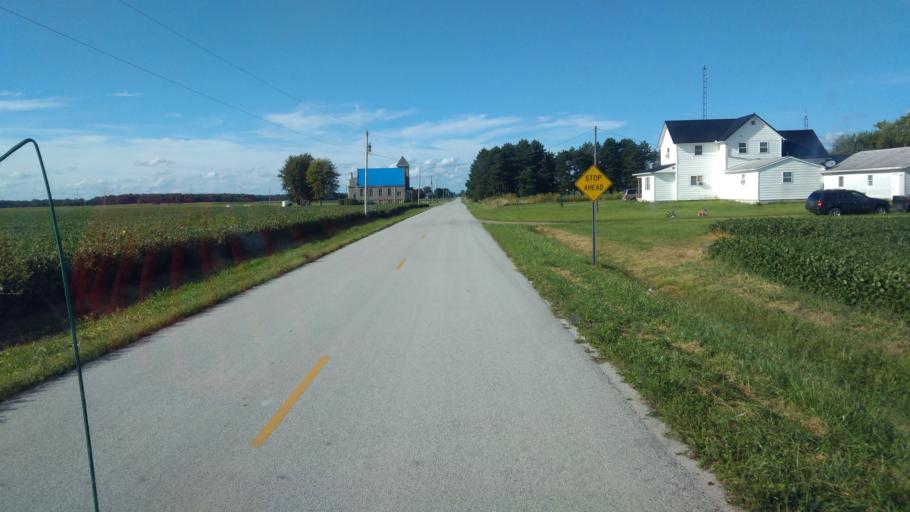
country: US
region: Ohio
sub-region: Hardin County
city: Kenton
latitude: 40.7442
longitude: -83.6906
